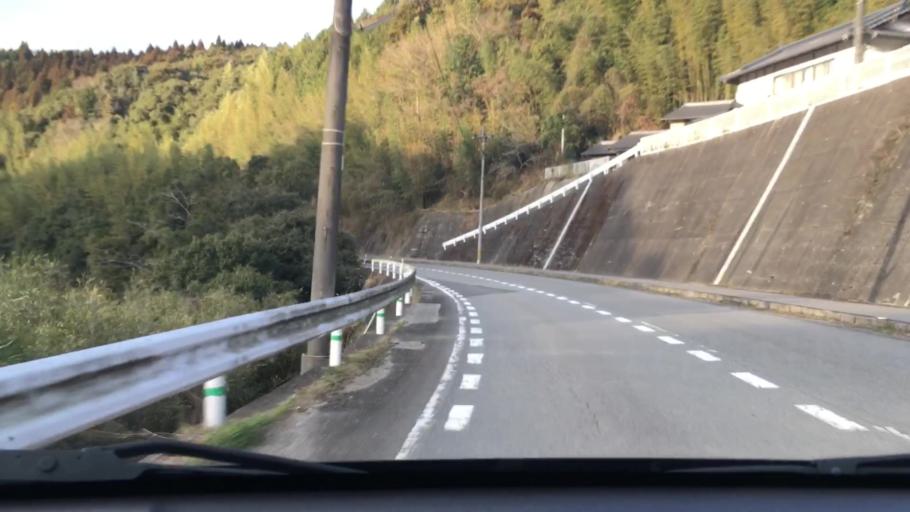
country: JP
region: Oita
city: Hiji
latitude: 33.4196
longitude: 131.4192
